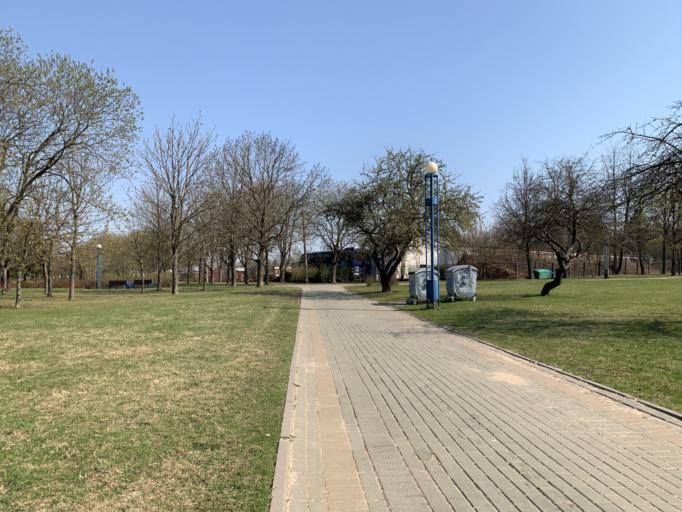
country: BY
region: Minsk
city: Borovlyany
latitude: 53.9375
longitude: 27.6565
